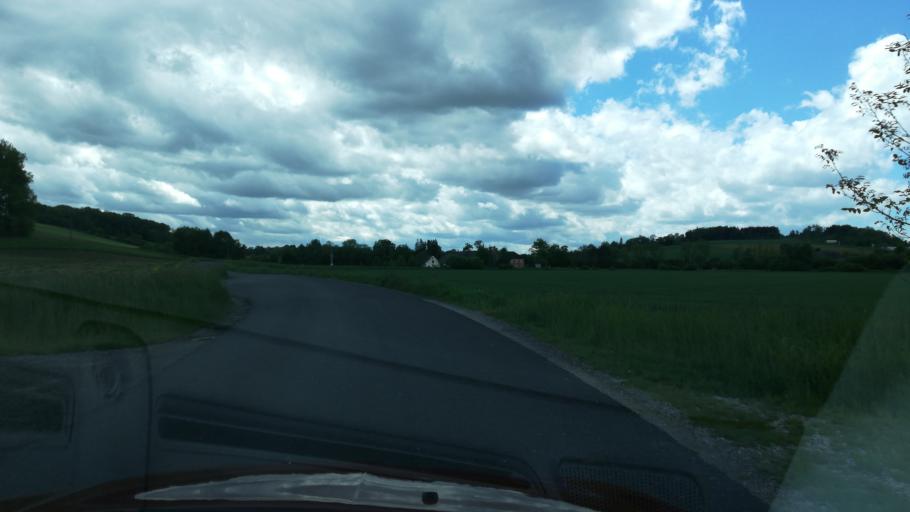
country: AT
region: Upper Austria
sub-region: Politischer Bezirk Linz-Land
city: Traun
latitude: 48.1896
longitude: 14.2342
